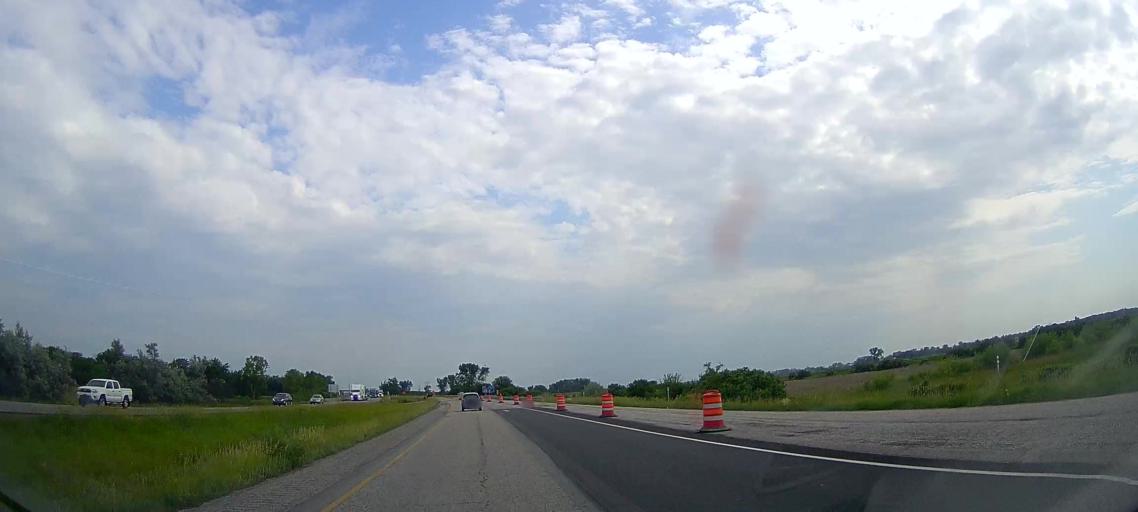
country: US
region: Nebraska
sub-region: Burt County
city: Tekamah
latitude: 41.7373
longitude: -96.0484
